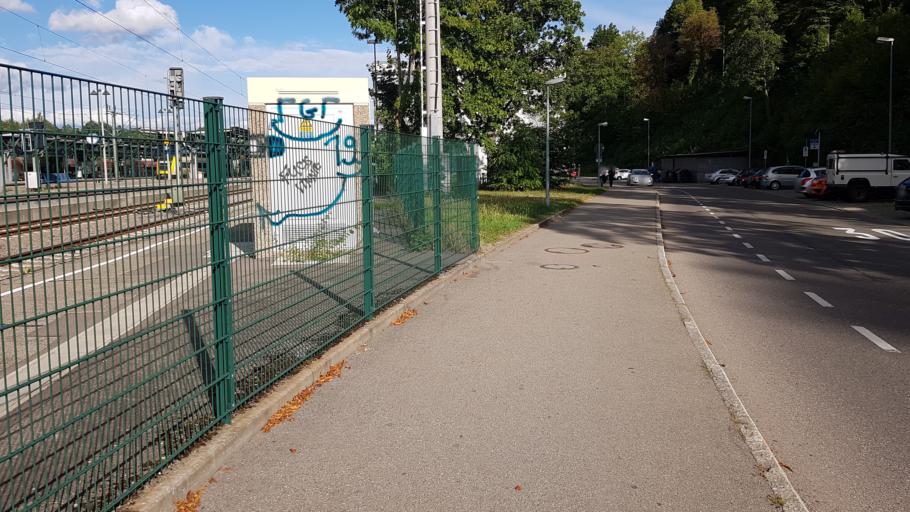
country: DE
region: Baden-Wuerttemberg
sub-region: Freiburg Region
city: Rottweil
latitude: 48.1650
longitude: 8.6367
